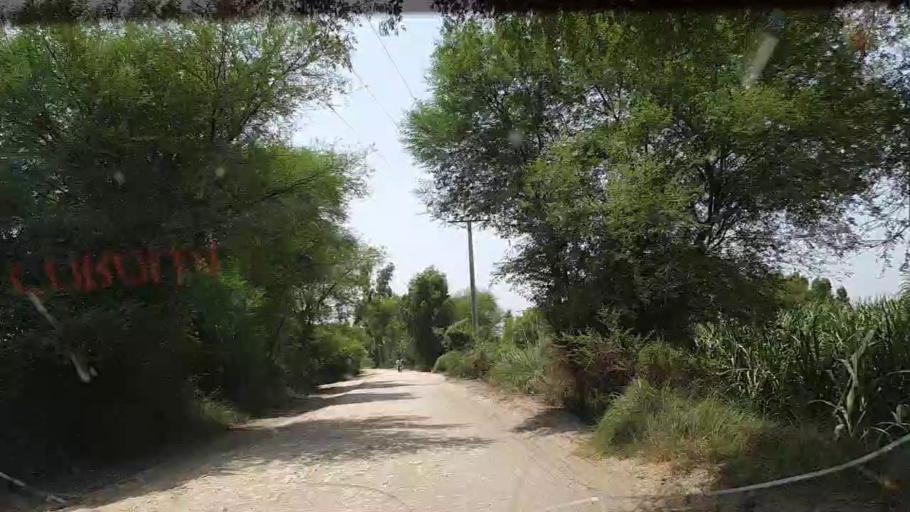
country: PK
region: Sindh
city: Ghotki
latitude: 28.0825
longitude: 69.3161
